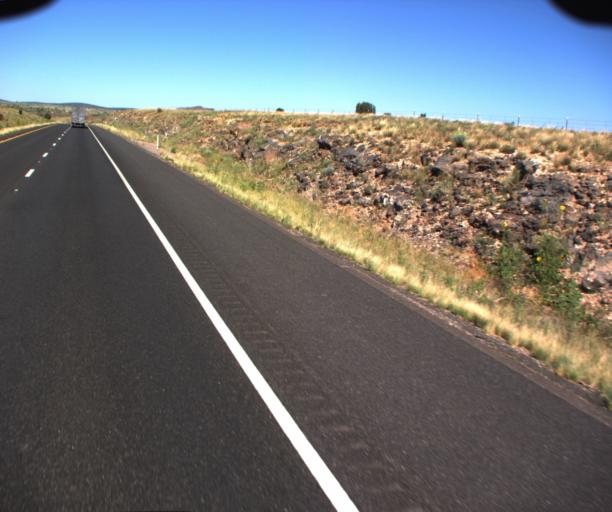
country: US
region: Arizona
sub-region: Yavapai County
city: Paulden
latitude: 35.2350
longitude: -112.6291
